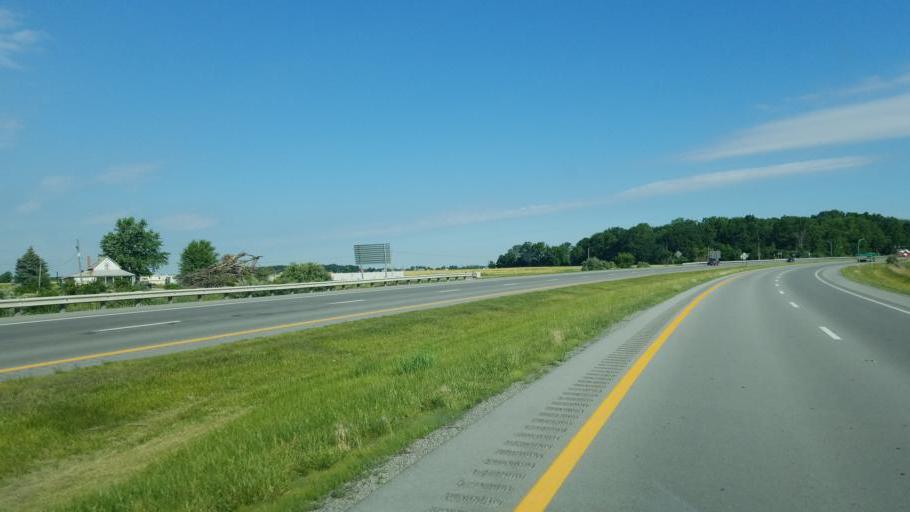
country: US
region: Ohio
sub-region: Hancock County
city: Findlay
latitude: 41.0006
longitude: -83.6582
